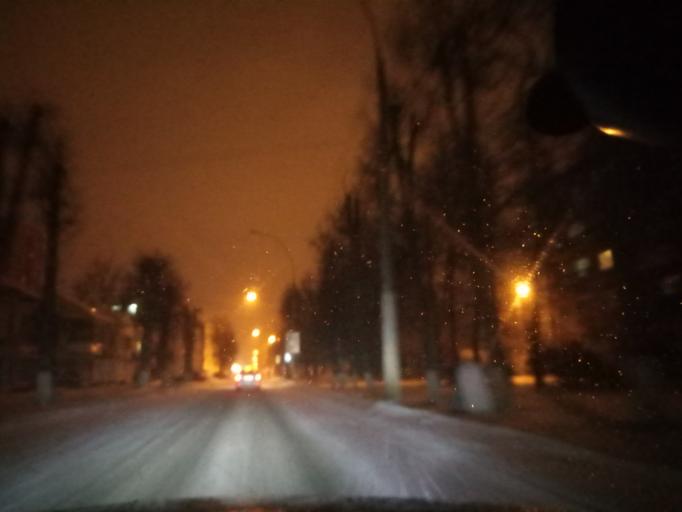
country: RU
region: Tula
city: Novomoskovsk
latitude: 54.0091
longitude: 38.2873
